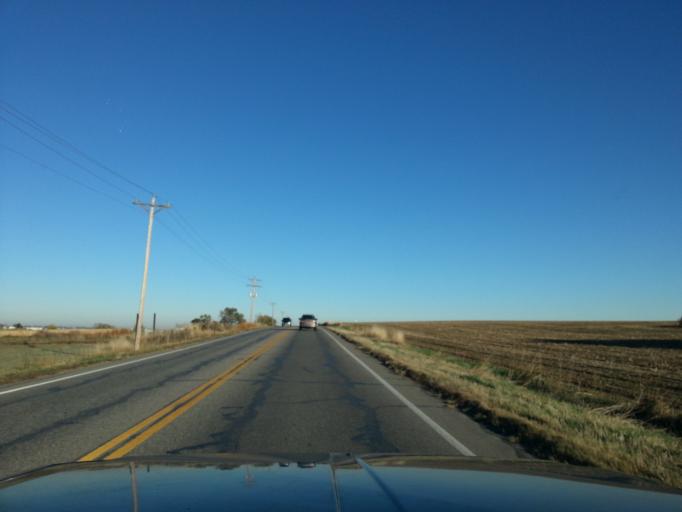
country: US
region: Colorado
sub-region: Larimer County
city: Loveland
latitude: 40.3781
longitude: -105.0022
